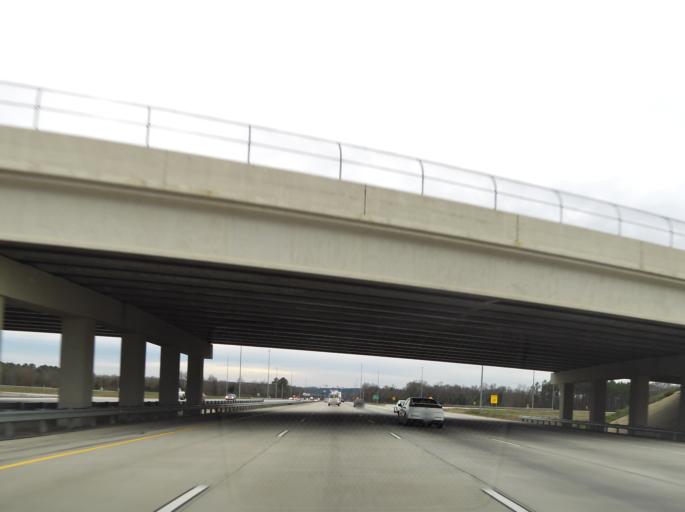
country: US
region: Georgia
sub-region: Peach County
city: Byron
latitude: 32.7169
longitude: -83.7297
